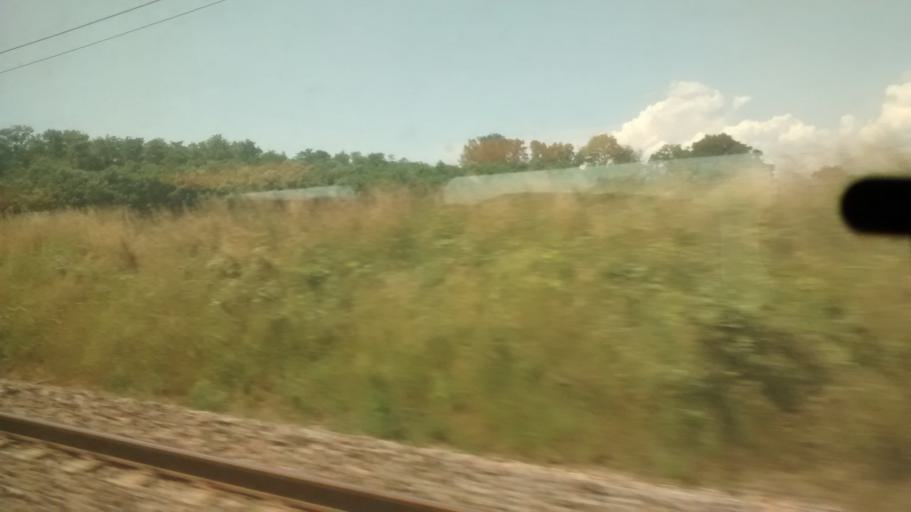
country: FR
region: Rhone-Alpes
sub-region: Departement de l'Ain
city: Saint-Etienne-sur-Chalaronne
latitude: 46.1353
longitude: 4.8424
